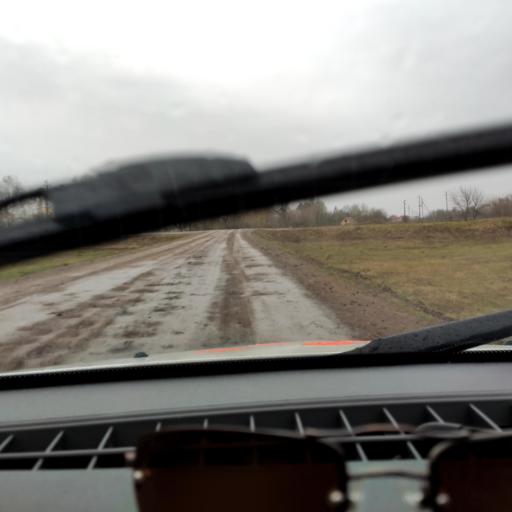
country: RU
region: Bashkortostan
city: Kabakovo
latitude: 54.5629
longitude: 56.0492
